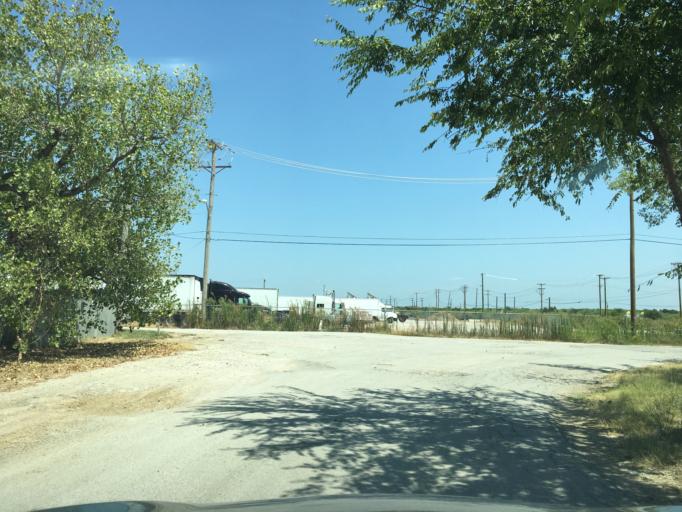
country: US
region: Texas
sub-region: Tarrant County
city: Crowley
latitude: 32.6147
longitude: -97.3535
